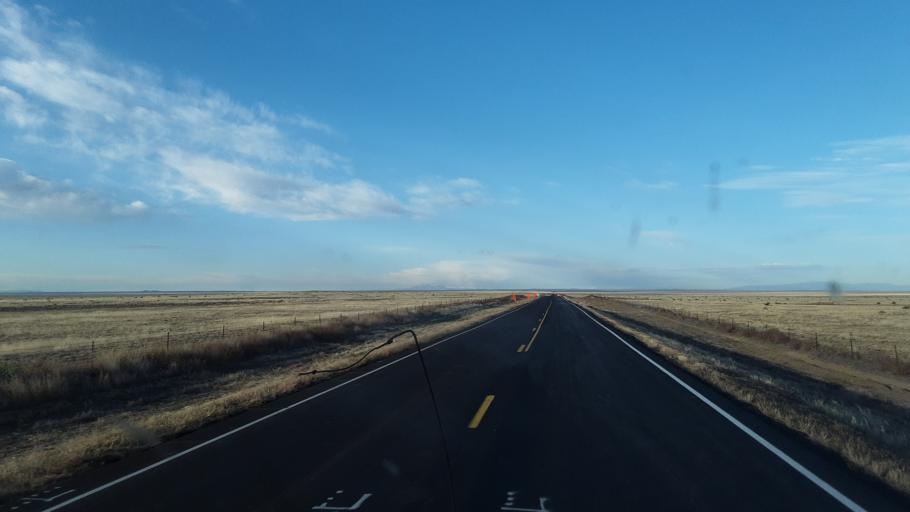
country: US
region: Colorado
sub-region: Otero County
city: Rocky Ford
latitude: 37.9679
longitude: -103.8271
